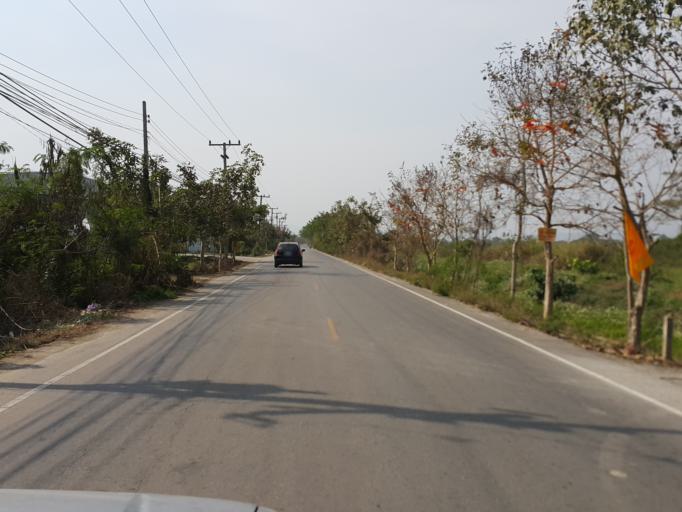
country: TH
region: Chiang Mai
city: Hang Dong
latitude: 18.6842
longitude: 98.9730
